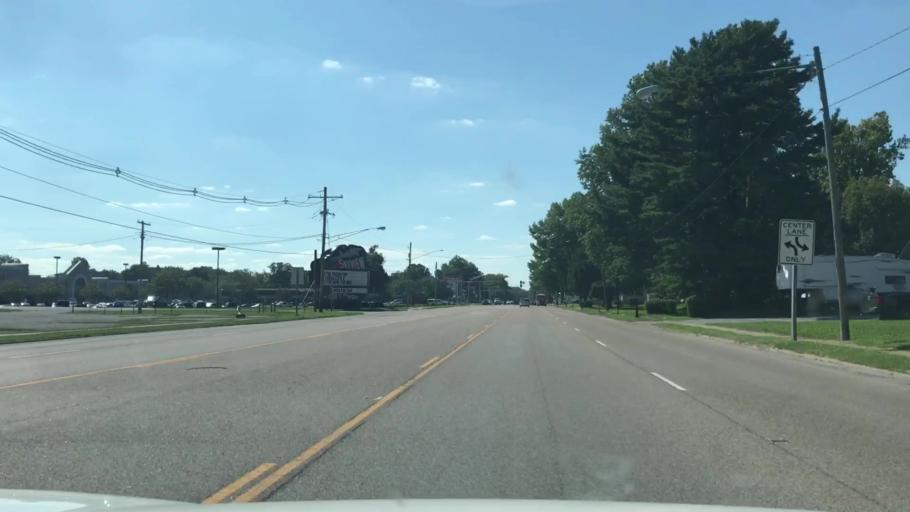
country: US
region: Illinois
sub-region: Saint Clair County
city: Swansea
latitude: 38.5417
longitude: -90.0321
